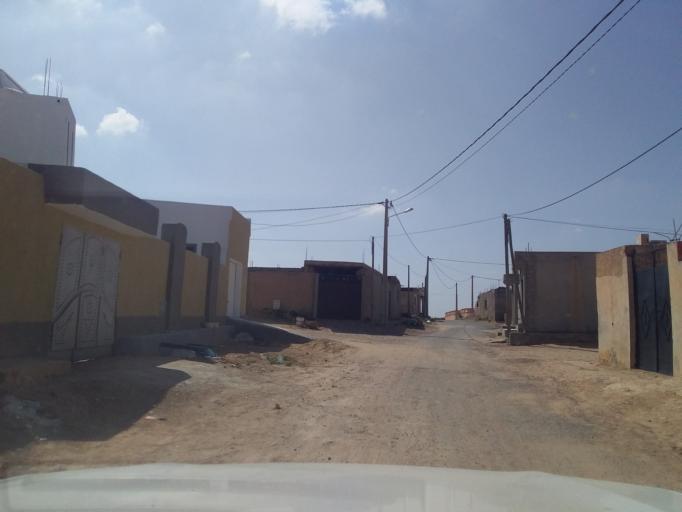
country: TN
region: Madanin
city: Medenine
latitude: 33.5806
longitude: 10.3235
